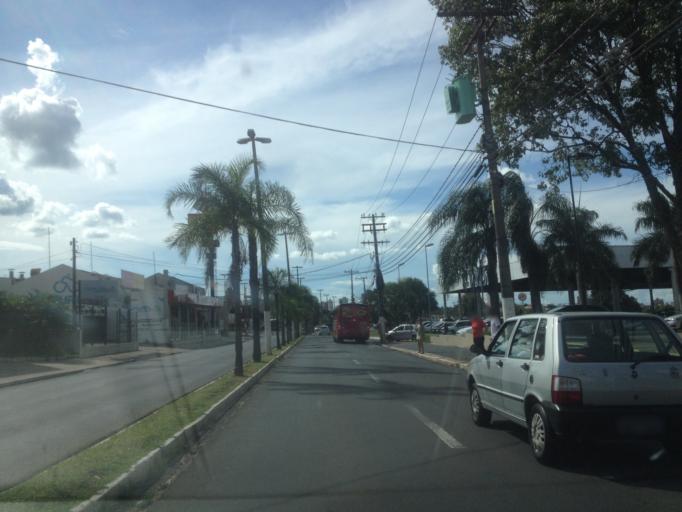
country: BR
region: Sao Paulo
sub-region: Marilia
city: Marilia
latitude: -22.2268
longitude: -49.9332
